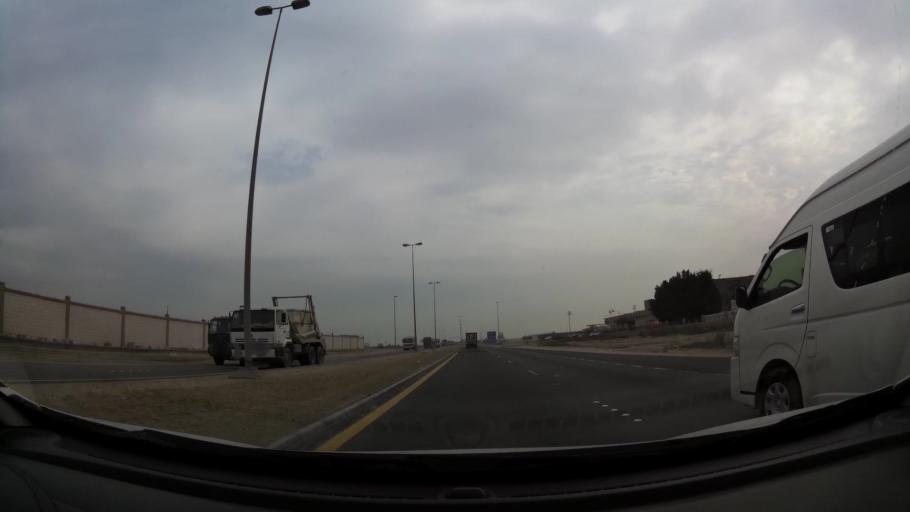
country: BH
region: Northern
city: Sitrah
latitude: 26.0781
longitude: 50.6137
